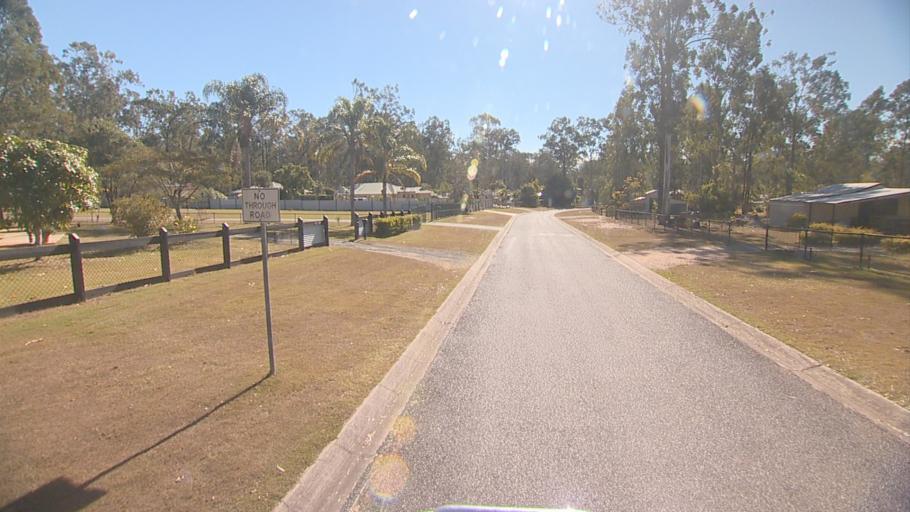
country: AU
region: Queensland
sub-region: Logan
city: North Maclean
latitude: -27.8178
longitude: 152.9466
